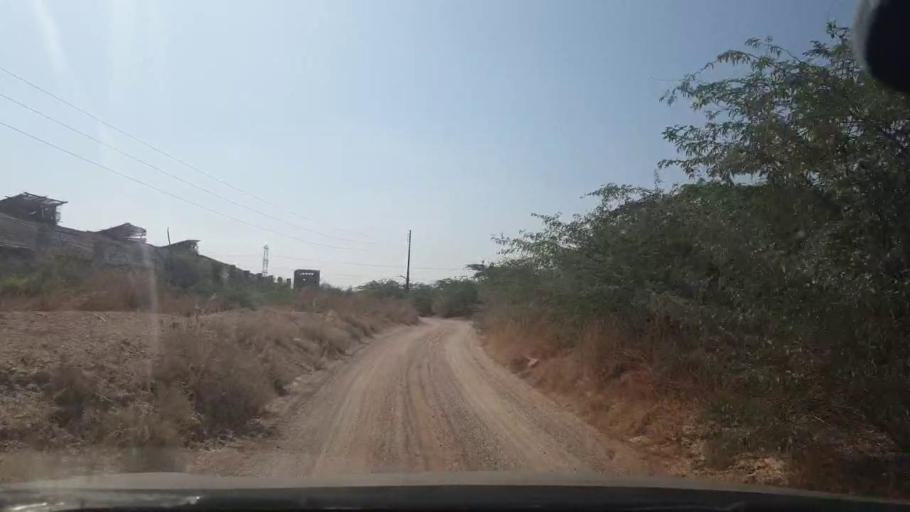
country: PK
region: Sindh
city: Malir Cantonment
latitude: 25.1671
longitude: 67.2046
